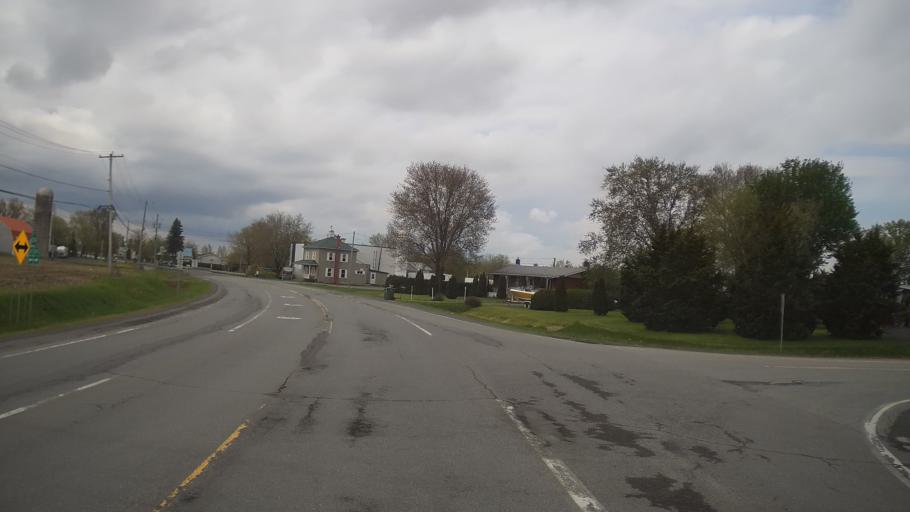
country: CA
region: Quebec
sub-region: Monteregie
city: Saint-Jean-sur-Richelieu
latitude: 45.3239
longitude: -73.1856
